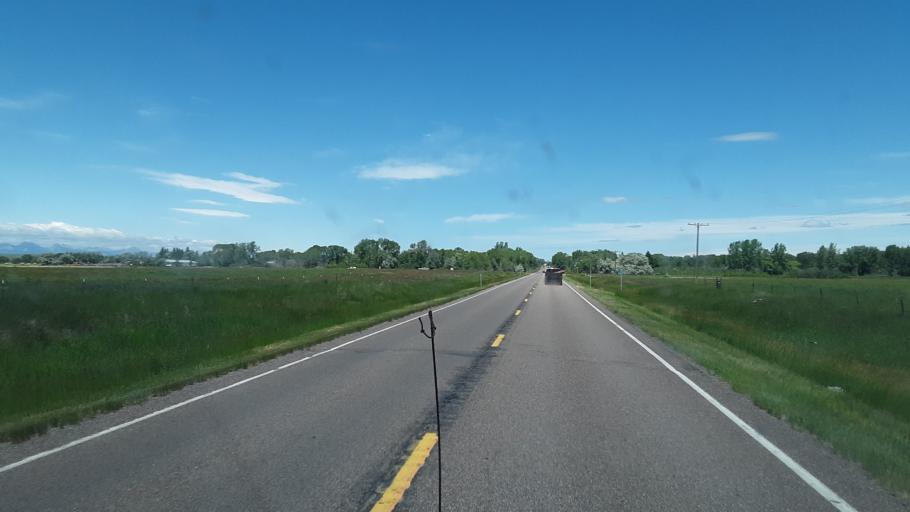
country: US
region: Montana
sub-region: Teton County
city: Choteau
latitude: 47.7829
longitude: -112.1582
